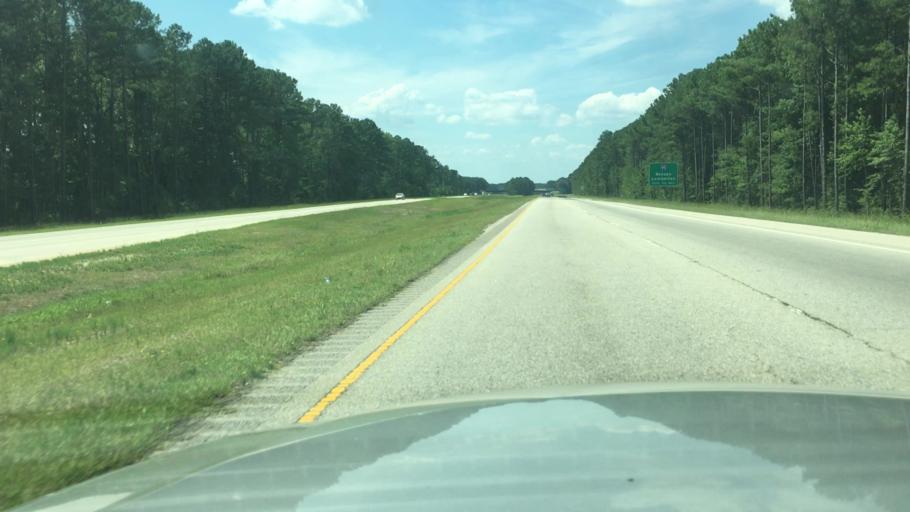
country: US
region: North Carolina
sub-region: Cumberland County
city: Vander
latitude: 34.9624
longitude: -78.8462
